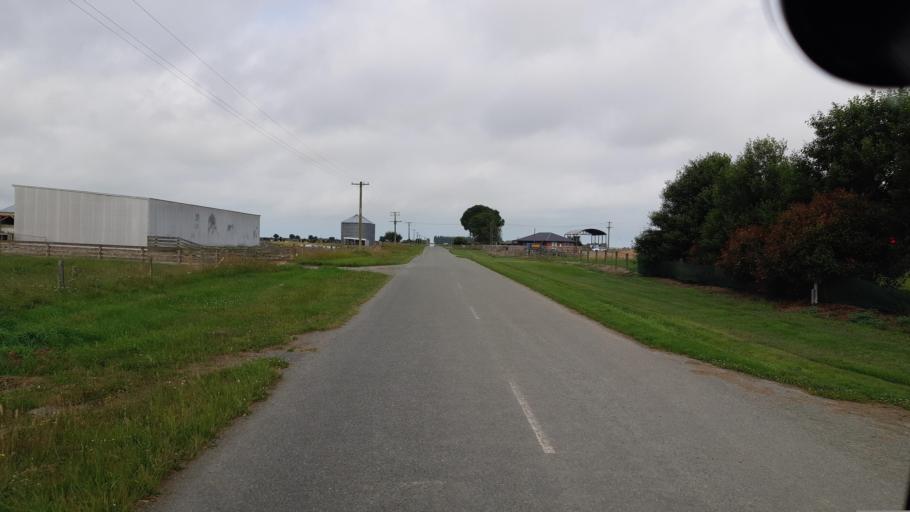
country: NZ
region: Canterbury
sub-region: Timaru District
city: Timaru
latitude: -44.2484
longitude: 171.3435
